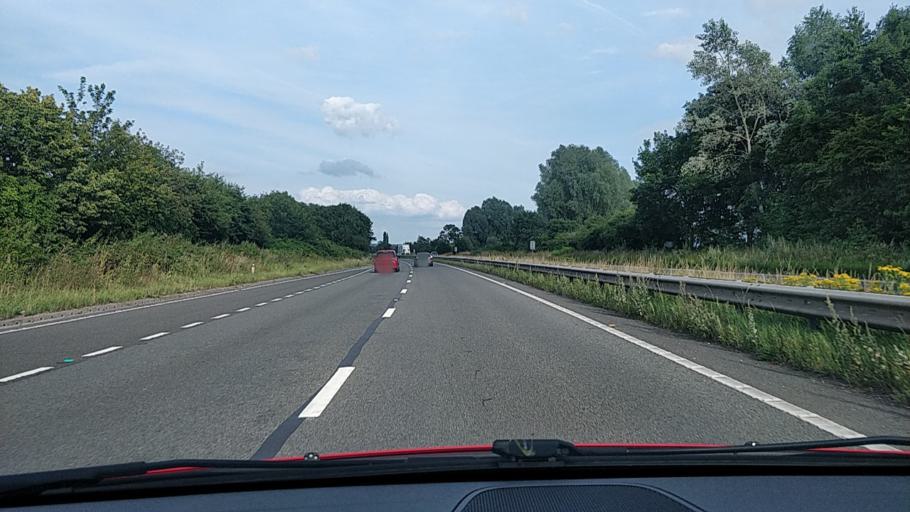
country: GB
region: Wales
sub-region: County of Flintshire
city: Hawarden
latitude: 53.1602
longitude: -3.0007
